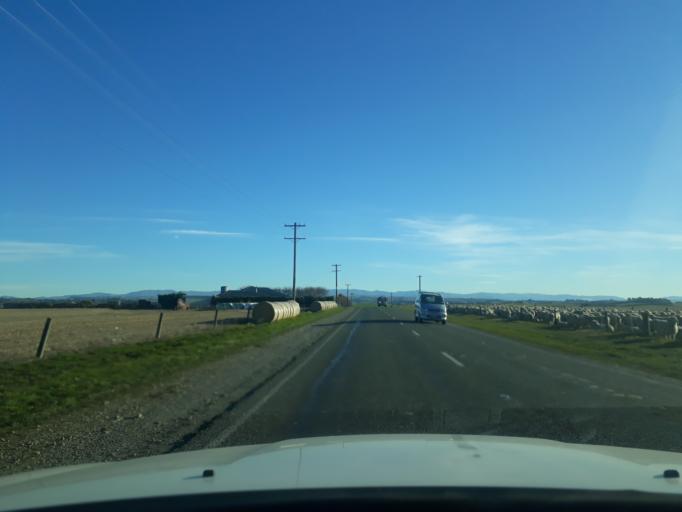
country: NZ
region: Canterbury
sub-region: Timaru District
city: Timaru
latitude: -44.3363
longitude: 171.2207
